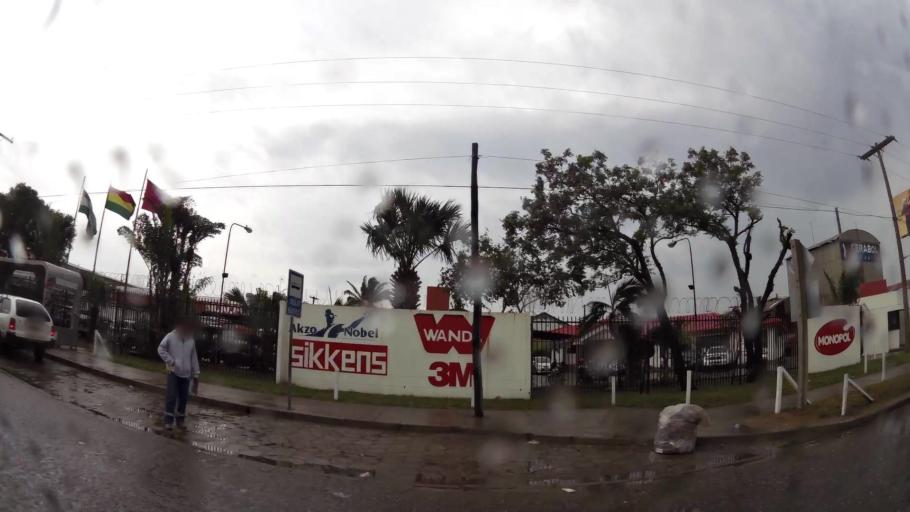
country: BO
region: Santa Cruz
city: Santa Cruz de la Sierra
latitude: -17.7871
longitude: -63.1483
